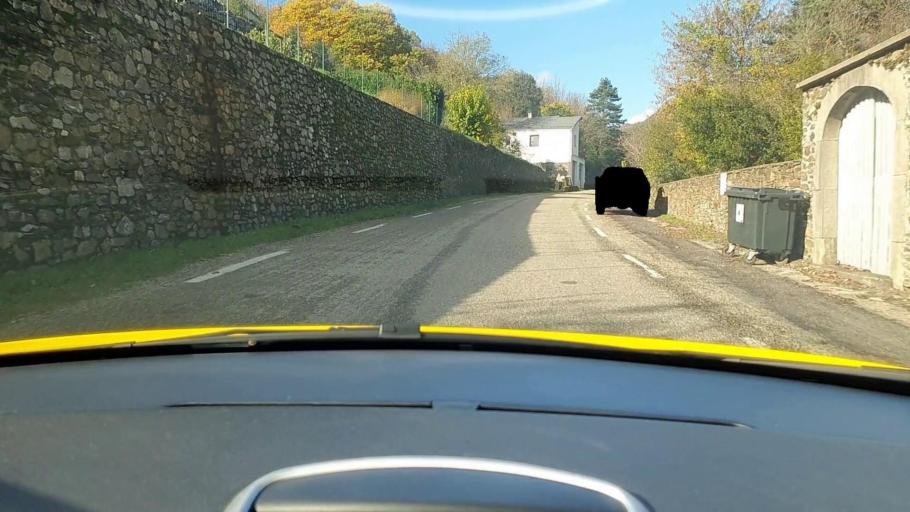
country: FR
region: Languedoc-Roussillon
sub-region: Departement du Gard
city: Valleraugue
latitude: 44.1580
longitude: 3.6777
